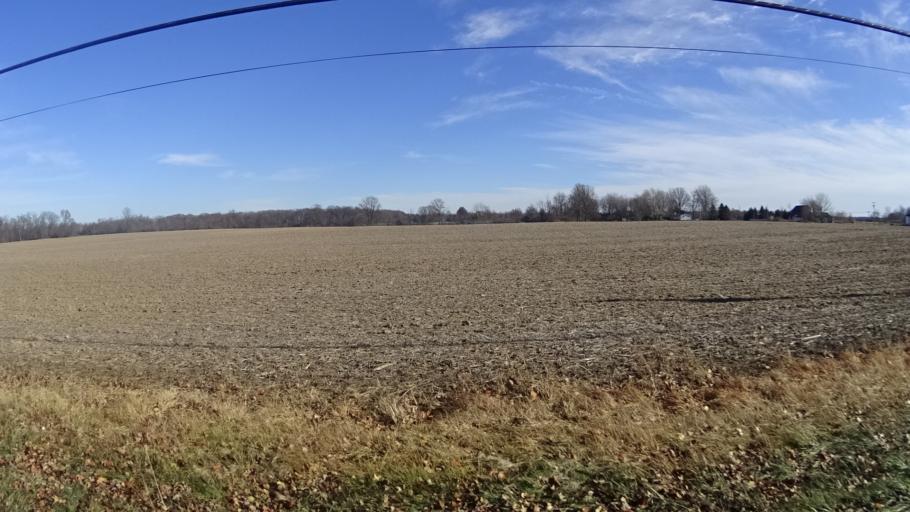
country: US
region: Ohio
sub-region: Huron County
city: Wakeman
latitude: 41.3217
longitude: -82.3439
